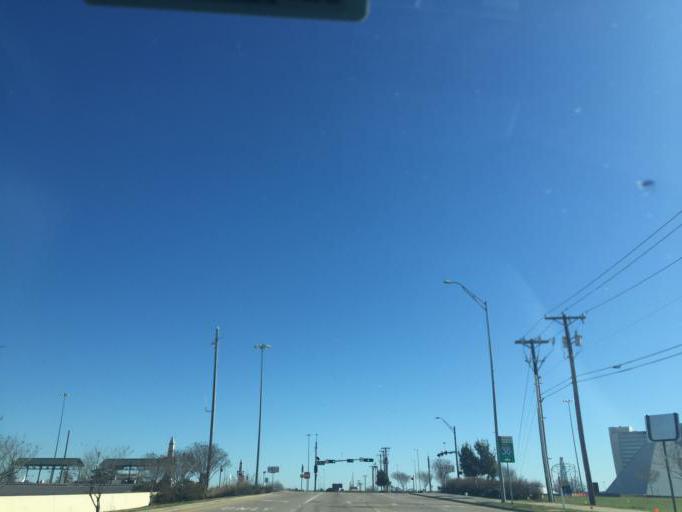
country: US
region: Texas
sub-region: Tarrant County
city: Arlington
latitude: 32.7591
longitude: -97.0865
